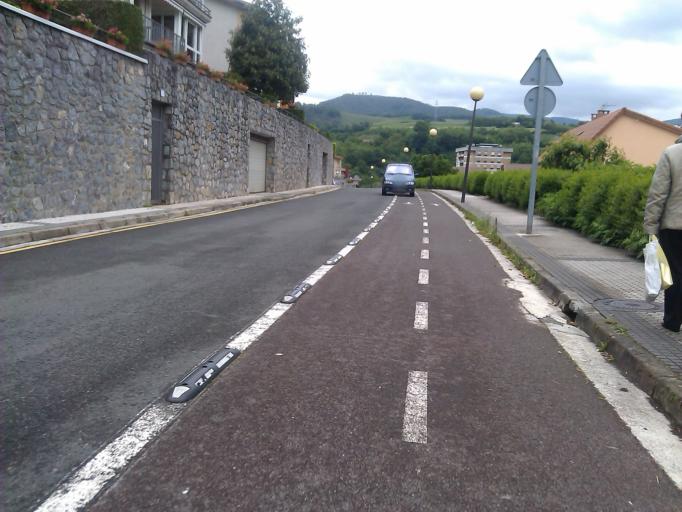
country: ES
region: Basque Country
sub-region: Provincia de Guipuzcoa
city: Andoain
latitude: 43.2158
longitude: -2.0195
